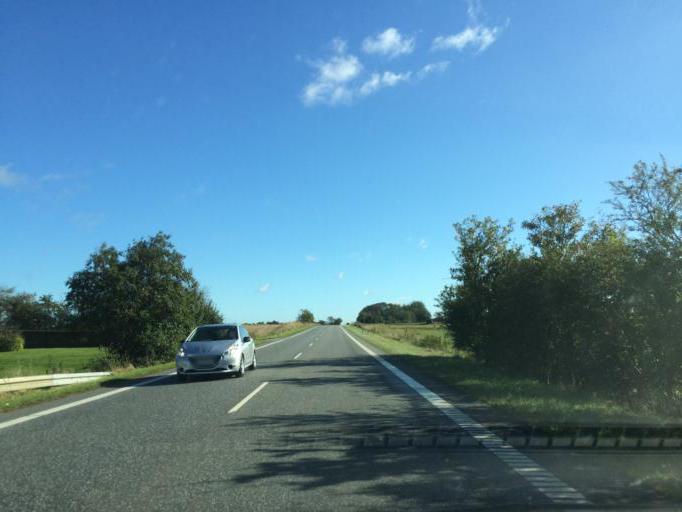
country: DK
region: Central Jutland
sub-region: Holstebro Kommune
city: Vinderup
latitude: 56.4007
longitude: 8.9265
